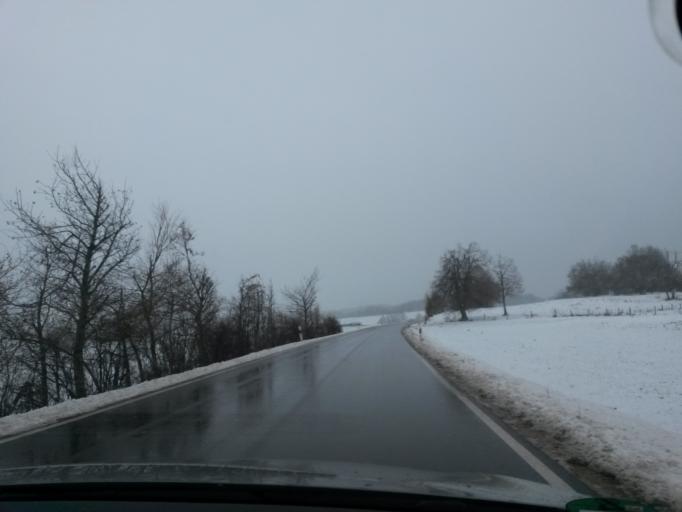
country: DE
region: Baden-Wuerttemberg
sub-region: Regierungsbezirk Stuttgart
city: Deggingen
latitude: 48.5830
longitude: 9.7387
